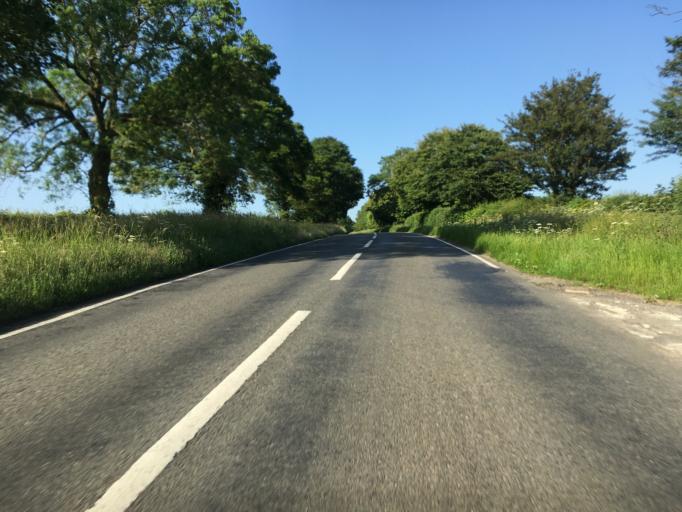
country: GB
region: England
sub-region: Oxfordshire
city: Charlbury
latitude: 51.9078
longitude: -1.4582
